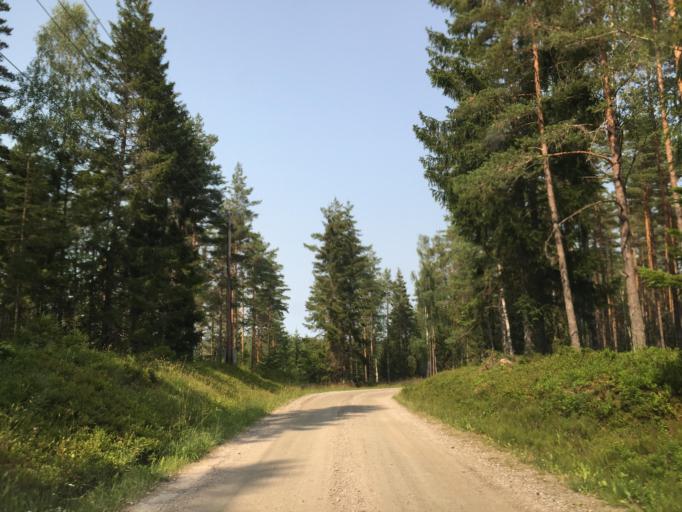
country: SE
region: Vaestra Goetaland
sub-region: Lilla Edets Kommun
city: Lilla Edet
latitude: 58.2522
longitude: 12.0900
